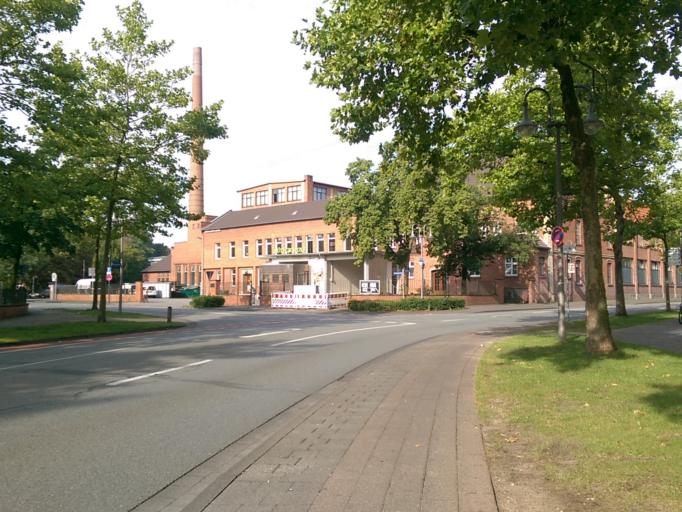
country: DE
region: North Rhine-Westphalia
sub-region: Regierungsbezirk Detmold
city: Guetersloh
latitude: 51.9041
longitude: 8.3729
